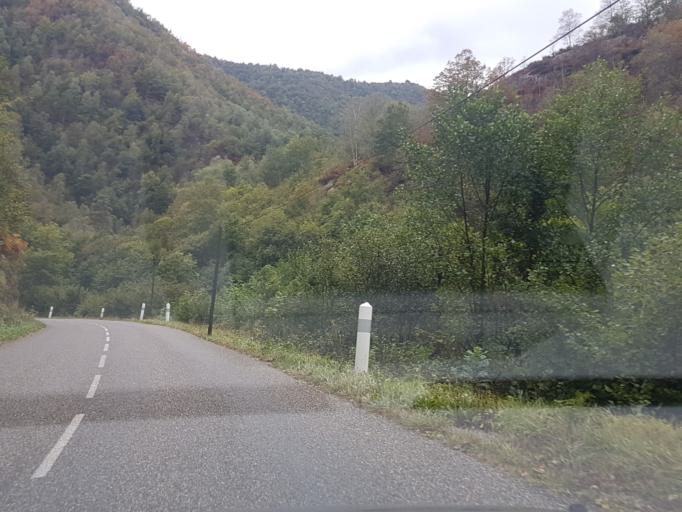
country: FR
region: Midi-Pyrenees
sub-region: Departement de l'Ariege
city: Saint-Girons
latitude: 42.9105
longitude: 1.2814
